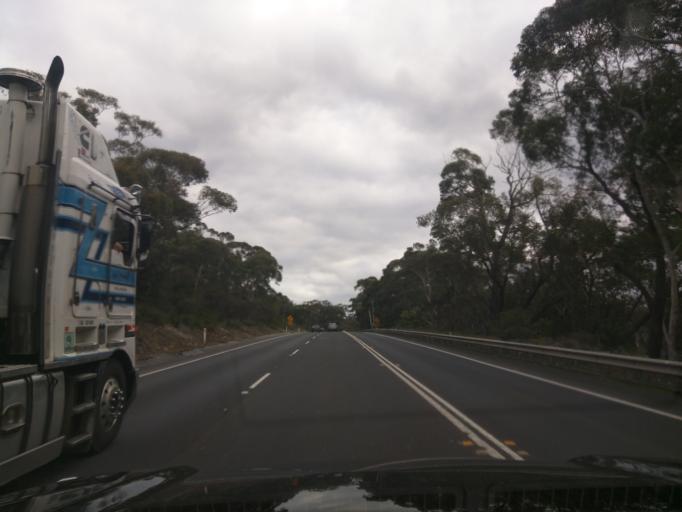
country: AU
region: New South Wales
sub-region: Wollongong
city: Mount Ousley
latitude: -34.3738
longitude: 150.8435
